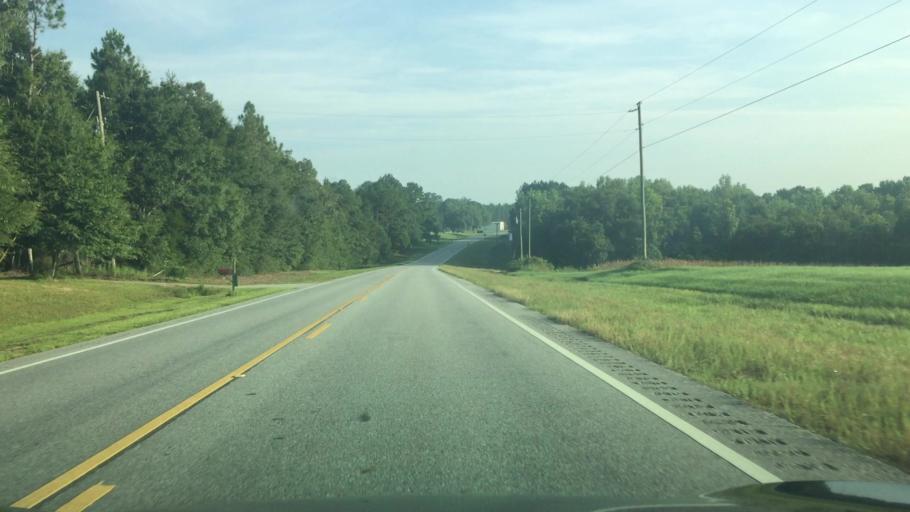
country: US
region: Alabama
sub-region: Covington County
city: Andalusia
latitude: 31.1353
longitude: -86.4590
